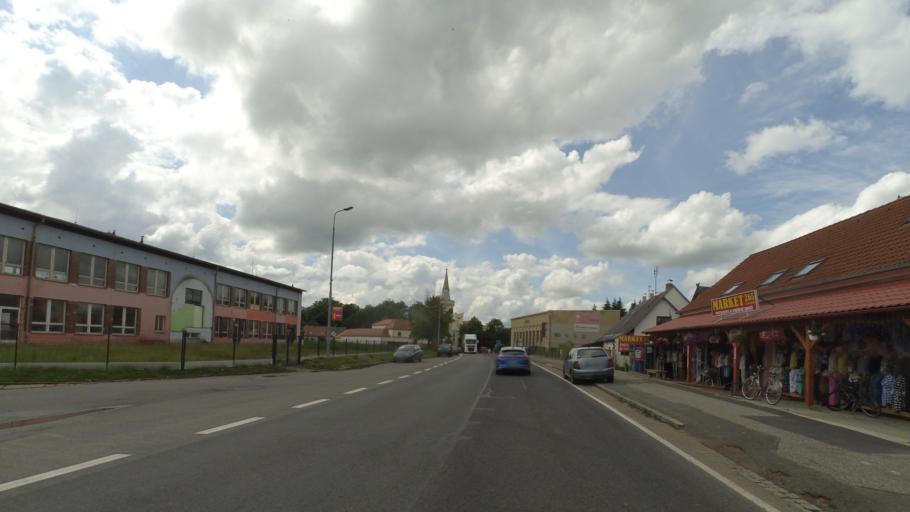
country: CZ
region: Plzensky
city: Bor
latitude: 49.7093
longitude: 12.7808
